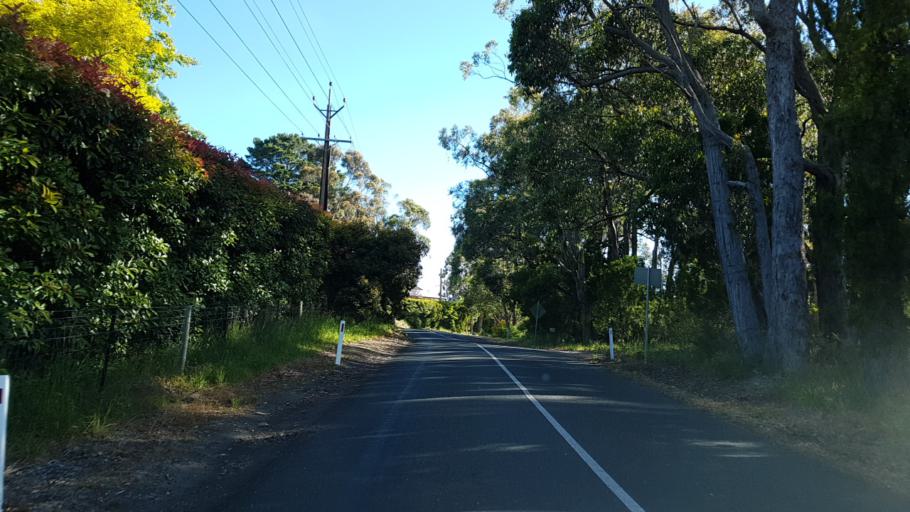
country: AU
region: South Australia
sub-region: Adelaide Hills
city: Adelaide Hills
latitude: -34.9375
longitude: 138.7415
